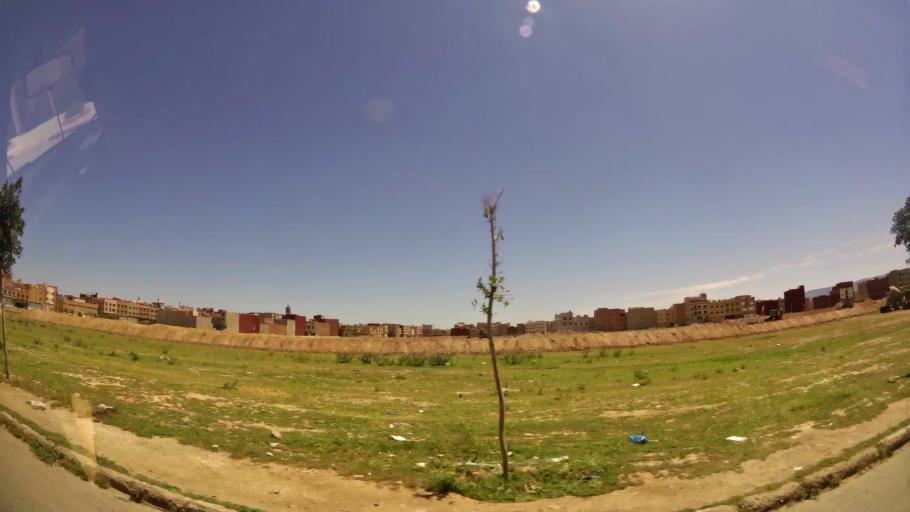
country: MA
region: Oriental
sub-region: Oujda-Angad
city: Oujda
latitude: 34.6733
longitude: -1.8824
